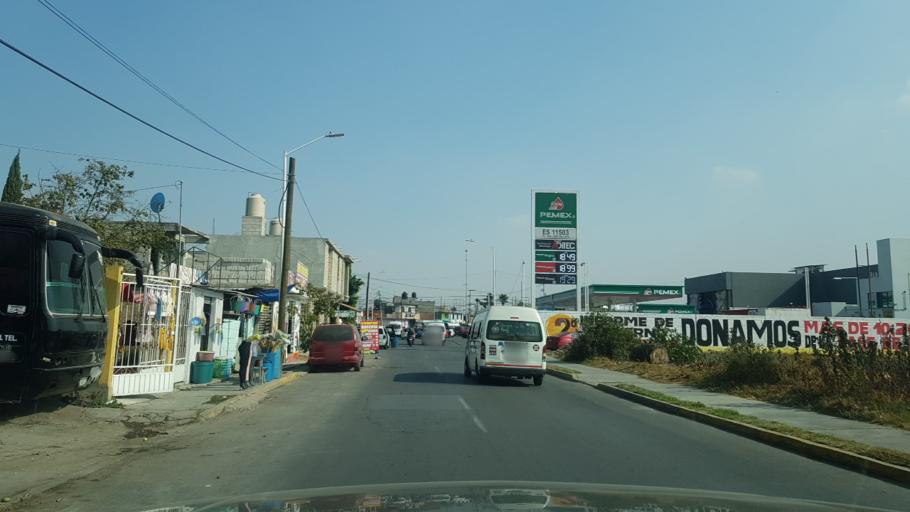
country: MX
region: Mexico
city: Santiago Teyahualco
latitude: 19.6571
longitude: -99.1234
